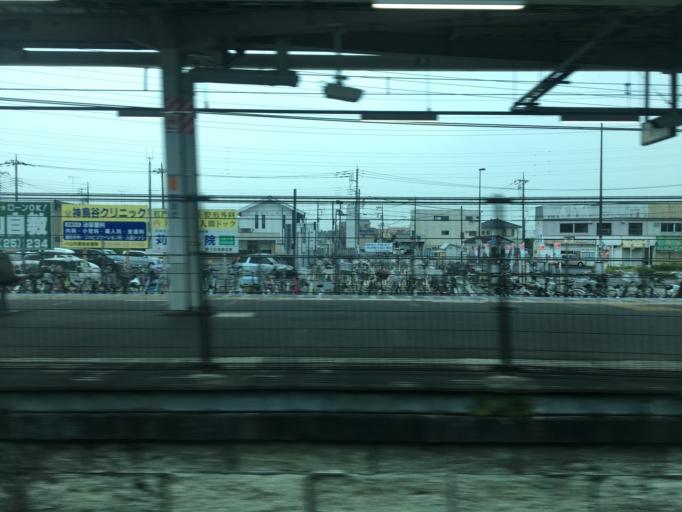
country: JP
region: Tochigi
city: Oyama
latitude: 36.2581
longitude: 139.7612
